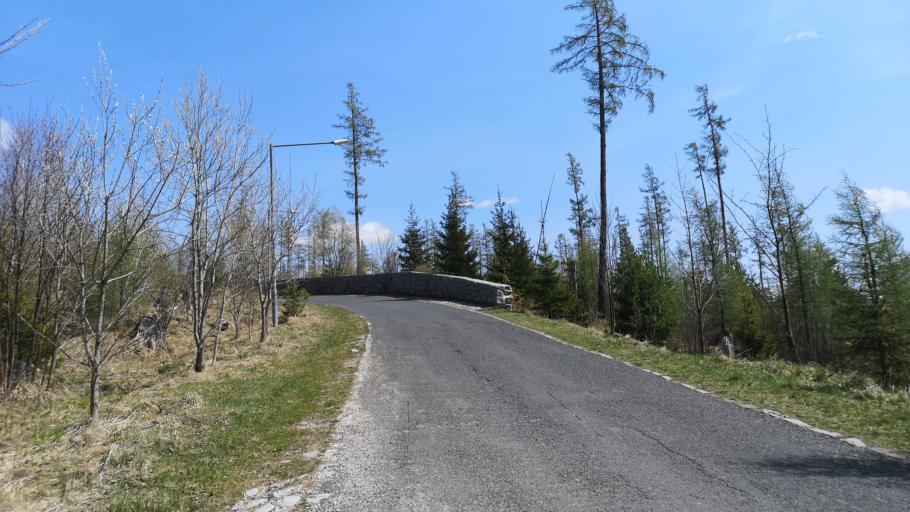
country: SK
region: Presovsky
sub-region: Okres Poprad
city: Vysoke Tatry
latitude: 49.1466
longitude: 20.2228
